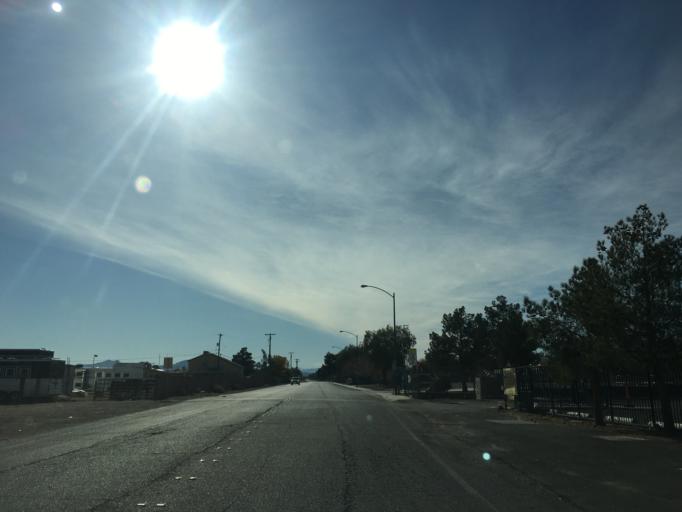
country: US
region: Nevada
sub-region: Clark County
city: Enterprise
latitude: 36.0025
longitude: -115.1659
